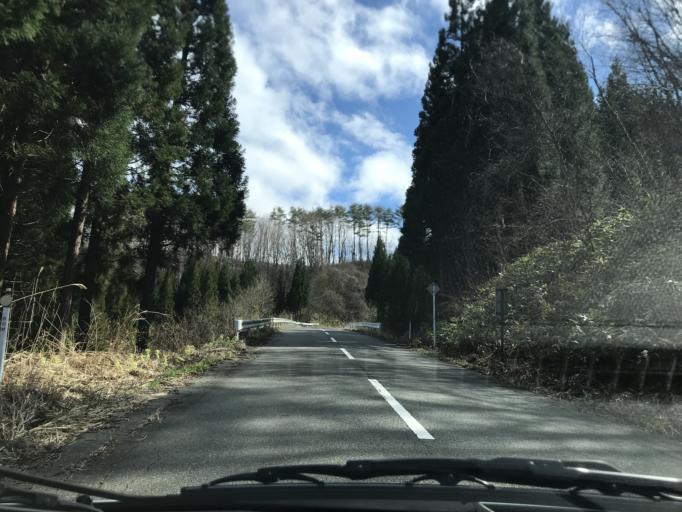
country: JP
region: Iwate
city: Mizusawa
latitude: 39.0685
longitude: 140.9824
